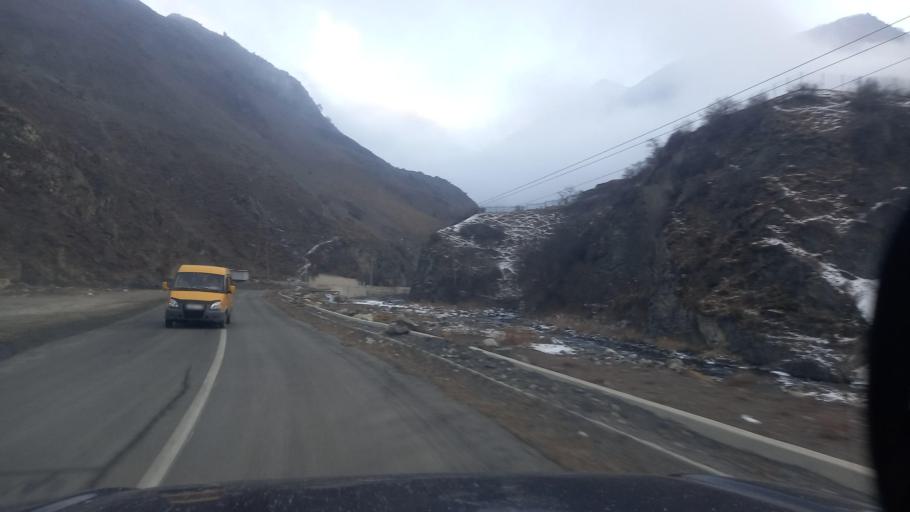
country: RU
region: Ingushetiya
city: Dzhayrakh
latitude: 42.7998
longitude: 44.7587
